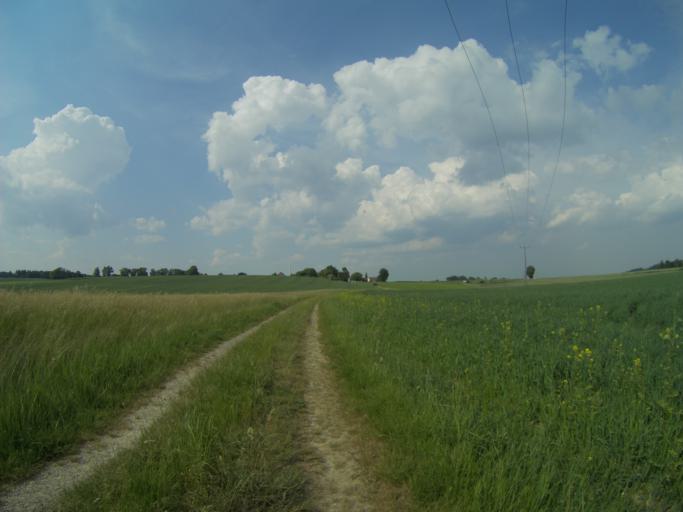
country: DE
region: Bavaria
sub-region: Upper Bavaria
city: Marzling
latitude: 48.4313
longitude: 11.7998
